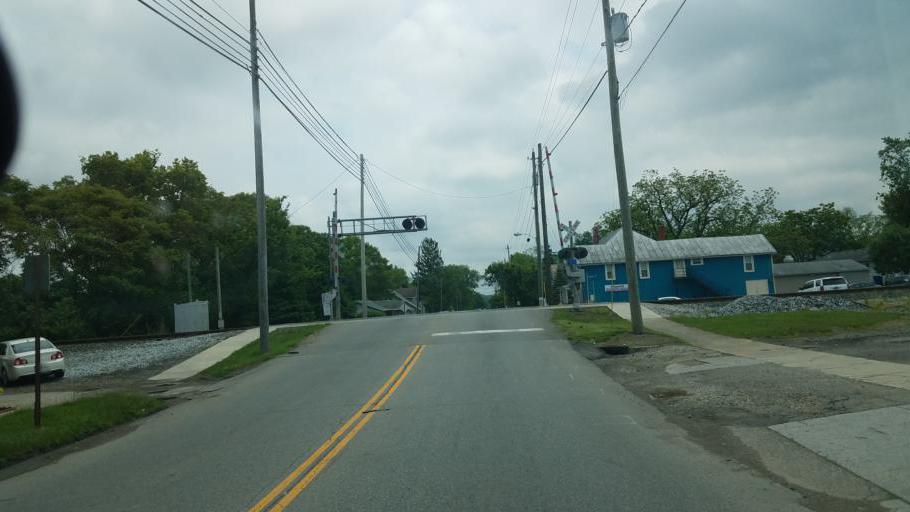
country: US
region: Ohio
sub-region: Delaware County
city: Delaware
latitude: 40.2995
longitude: -83.0830
